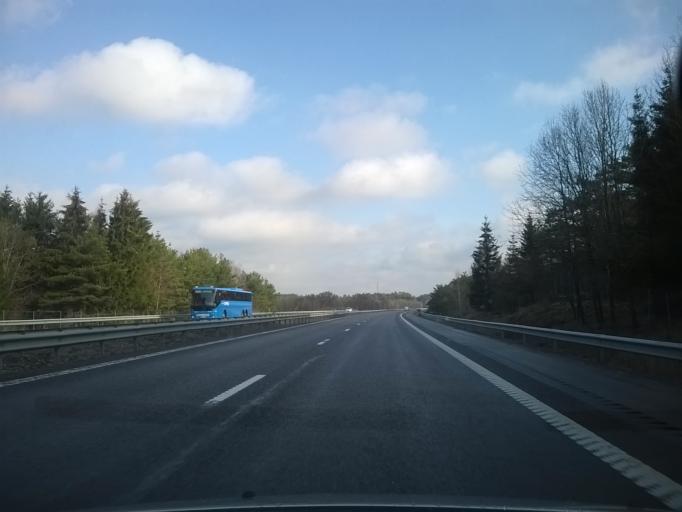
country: SE
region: Vaestra Goetaland
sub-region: Stenungsunds Kommun
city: Stora Hoga
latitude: 57.9938
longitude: 11.8424
